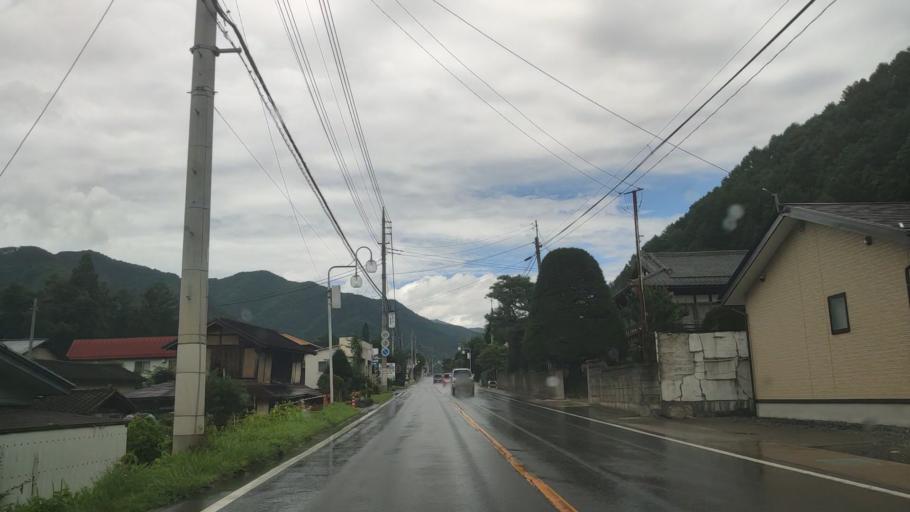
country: JP
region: Gunma
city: Numata
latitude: 36.7558
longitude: 139.2293
